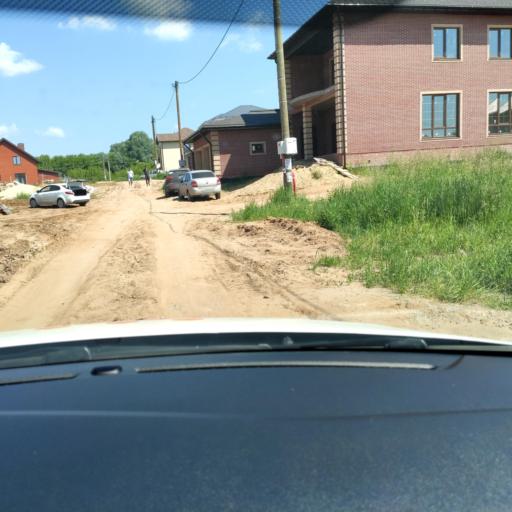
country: RU
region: Tatarstan
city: Vysokaya Gora
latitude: 55.7911
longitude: 49.2626
